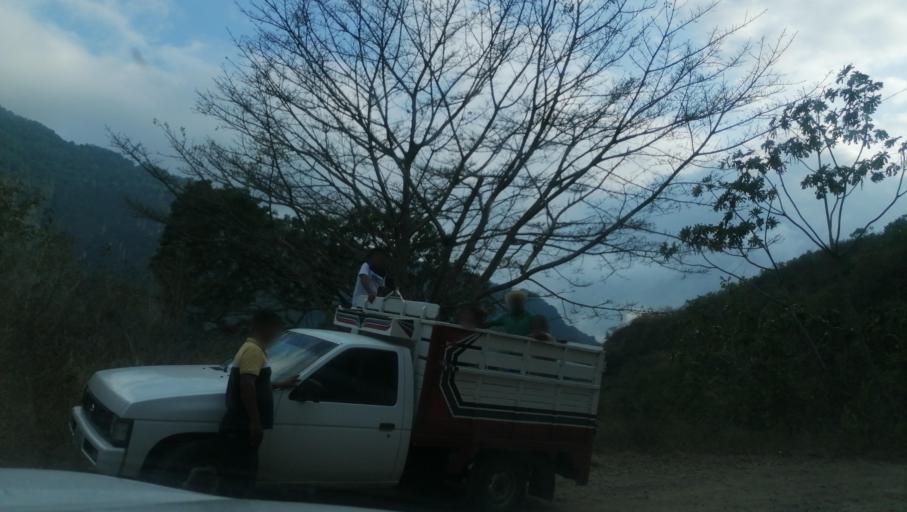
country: MX
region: Chiapas
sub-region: Cacahoatan
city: Benito Juarez
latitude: 15.1488
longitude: -92.1850
